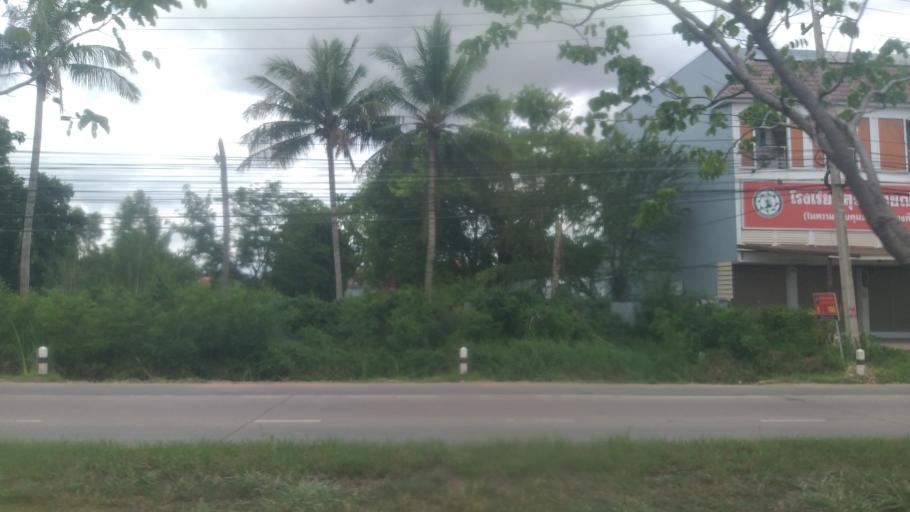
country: TH
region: Nakhon Ratchasima
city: Nakhon Ratchasima
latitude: 15.0472
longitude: 102.1315
